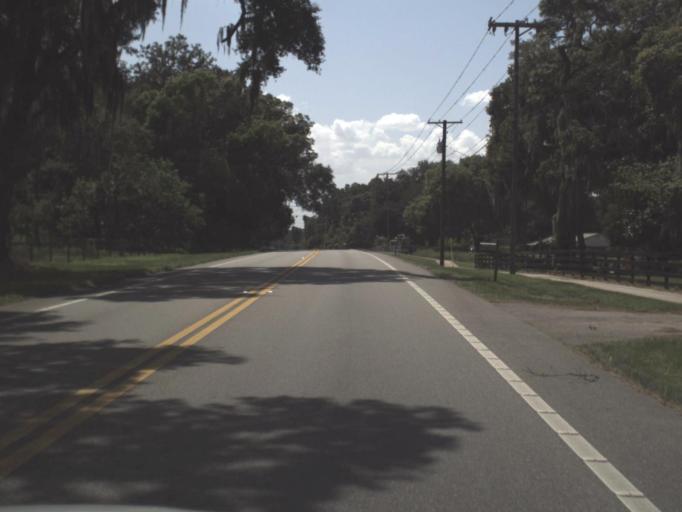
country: US
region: Florida
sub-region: Hillsborough County
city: Dover
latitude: 28.0221
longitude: -82.2179
